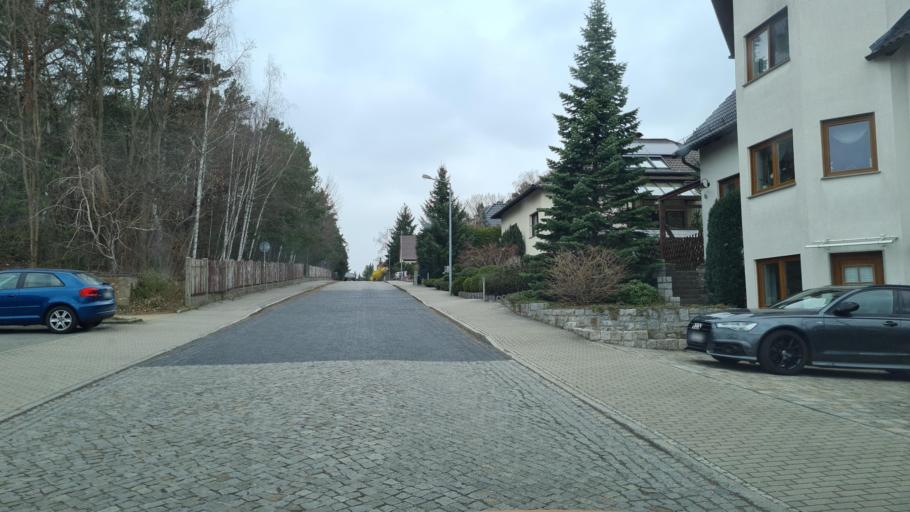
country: DE
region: Brandenburg
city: Lauchhammer
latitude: 51.4994
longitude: 13.7903
